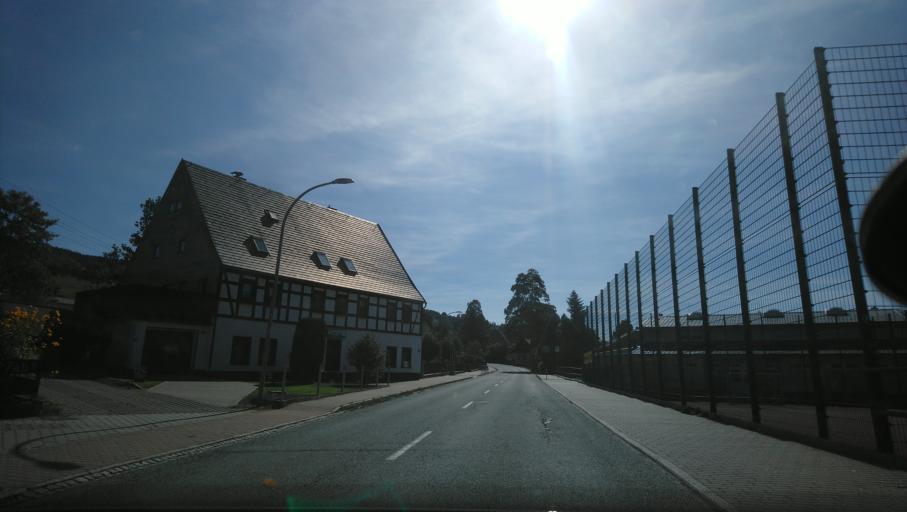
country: DE
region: Saxony
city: Konigswalde
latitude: 50.5454
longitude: 13.0496
